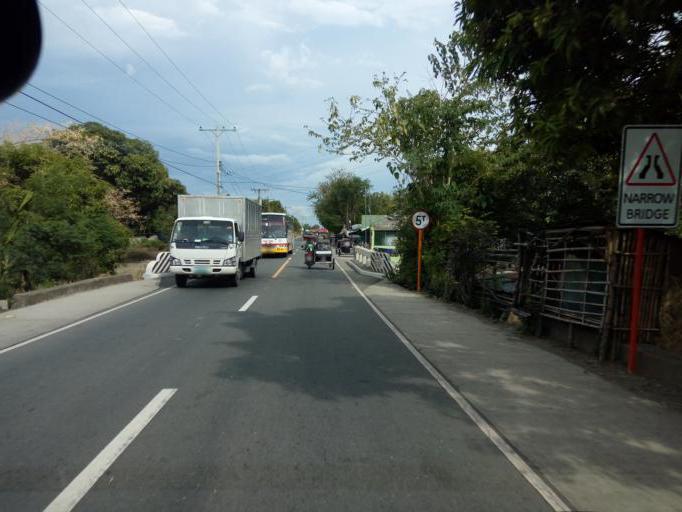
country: PH
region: Central Luzon
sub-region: Province of Nueva Ecija
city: Parista
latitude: 15.8215
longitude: 120.9547
